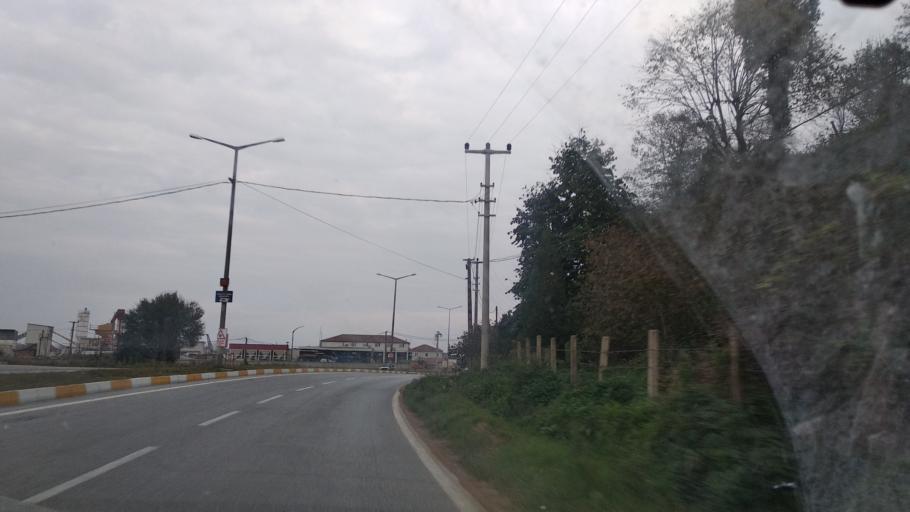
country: TR
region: Sakarya
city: Karasu
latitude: 41.1000
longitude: 30.6688
